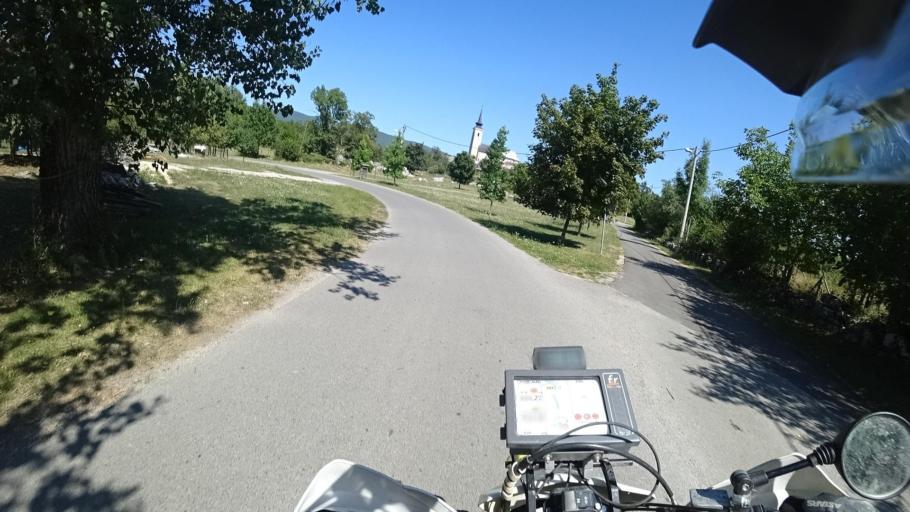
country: HR
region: Licko-Senjska
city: Popovaca
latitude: 44.7157
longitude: 15.2758
